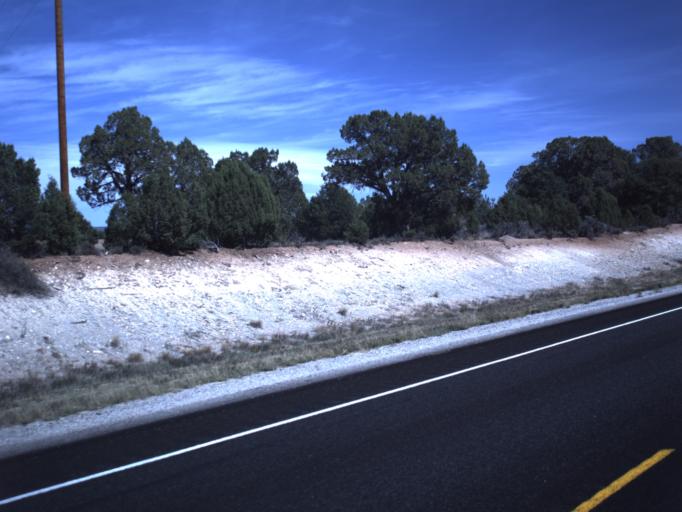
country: US
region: Colorado
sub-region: Dolores County
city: Dove Creek
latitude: 37.8265
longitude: -109.0768
